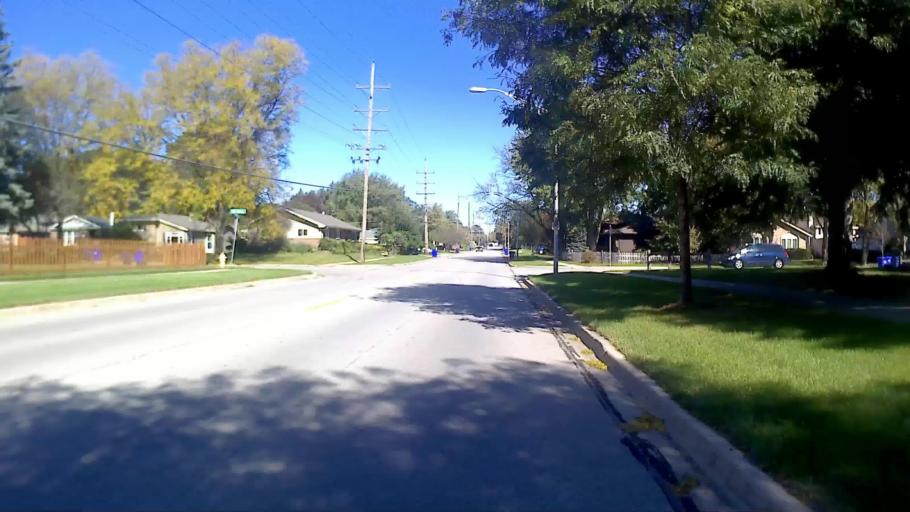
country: US
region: Illinois
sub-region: DuPage County
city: Wheaton
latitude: 41.8559
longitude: -88.0870
